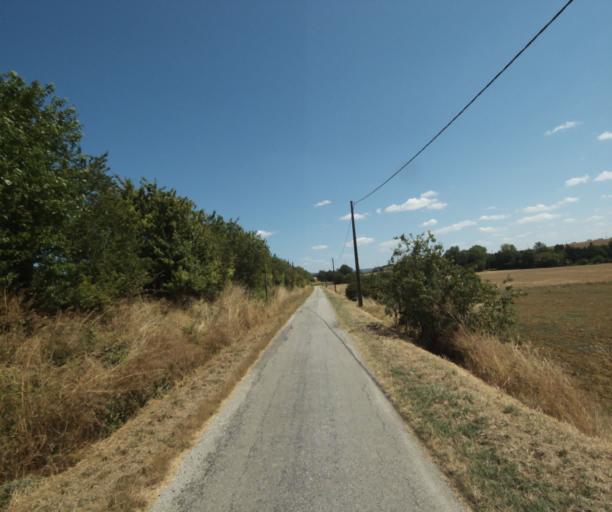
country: FR
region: Midi-Pyrenees
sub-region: Departement de la Haute-Garonne
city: Saint-Felix-Lauragais
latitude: 43.4859
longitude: 1.8965
